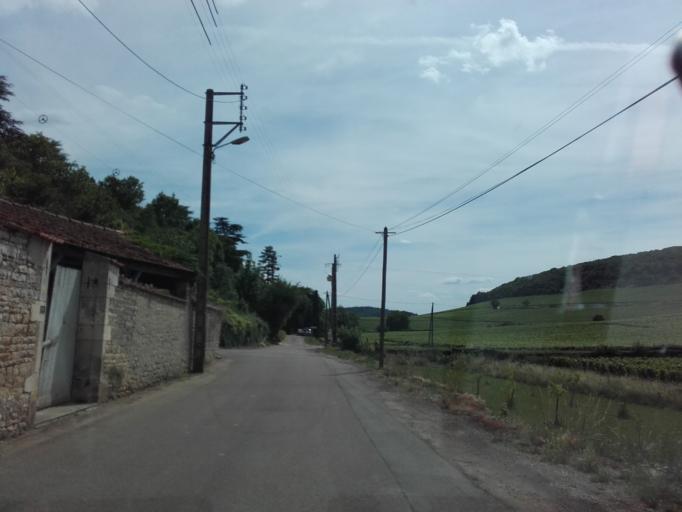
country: FR
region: Bourgogne
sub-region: Departement de Saone-et-Loire
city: Rully
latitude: 46.8732
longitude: 4.7350
